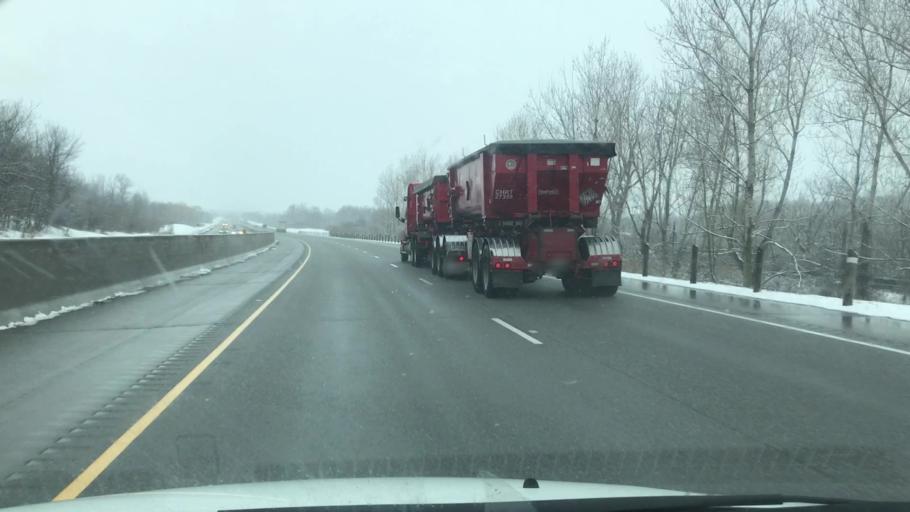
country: CA
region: Ontario
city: Kingston
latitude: 44.3153
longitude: -76.3833
